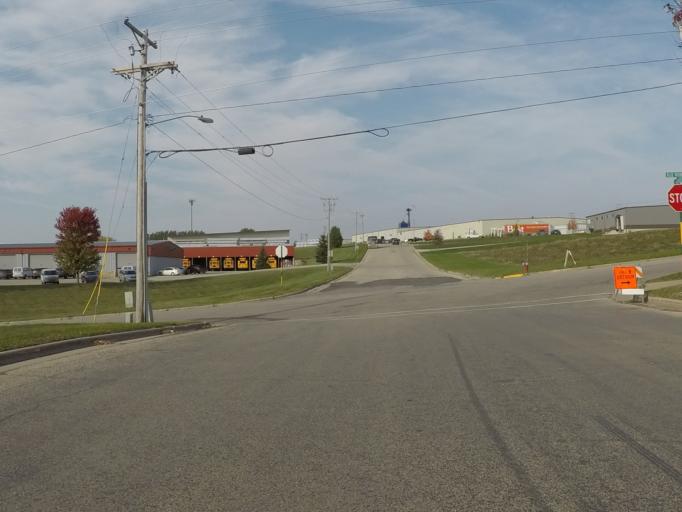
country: US
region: Wisconsin
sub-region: Dane County
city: Mount Horeb
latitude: 43.0055
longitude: -89.7449
